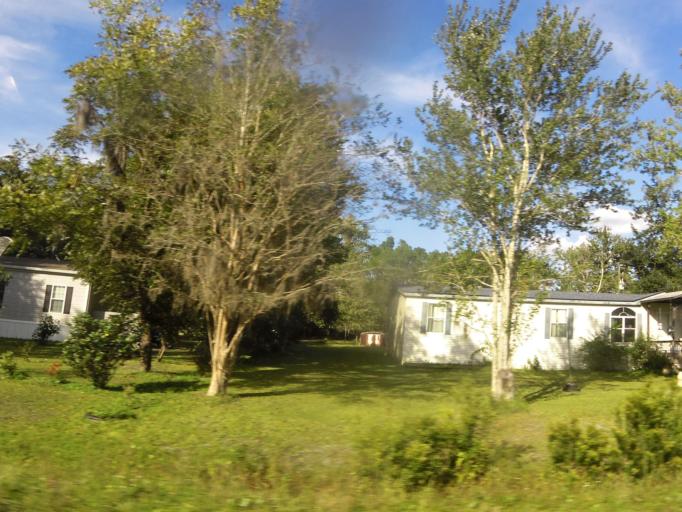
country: US
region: Florida
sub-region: Clay County
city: Green Cove Springs
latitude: 29.9196
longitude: -81.5457
